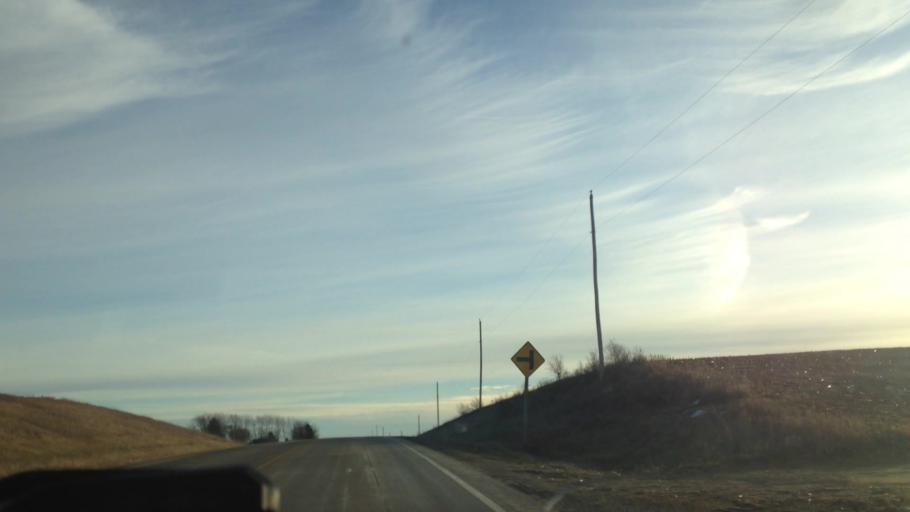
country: US
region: Wisconsin
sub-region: Dodge County
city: Theresa
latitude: 43.5364
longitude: -88.4583
